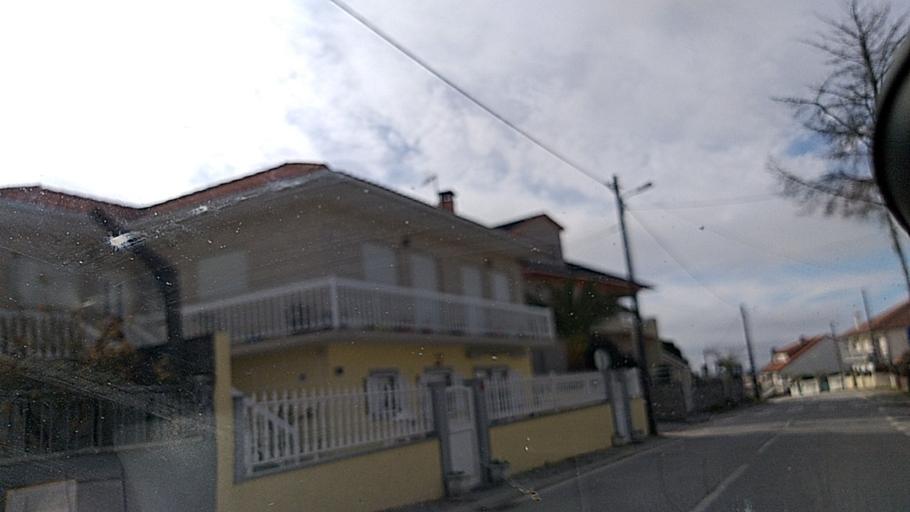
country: PT
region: Guarda
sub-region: Aguiar da Beira
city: Aguiar da Beira
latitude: 40.7810
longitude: -7.5181
